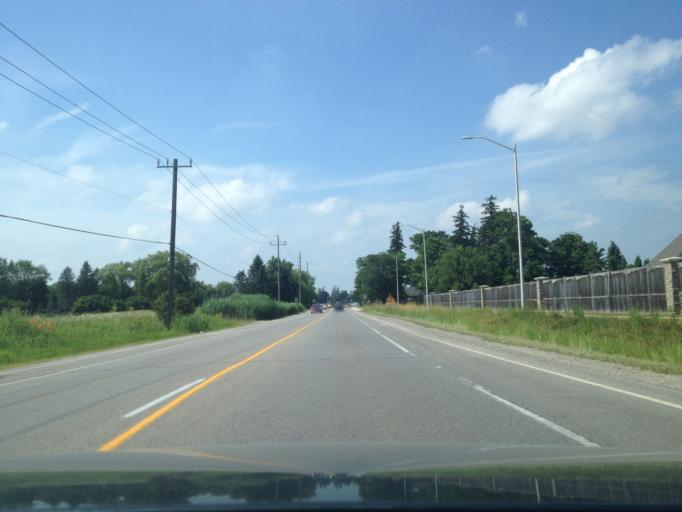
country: CA
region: Ontario
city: London
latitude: 43.0265
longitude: -81.3148
